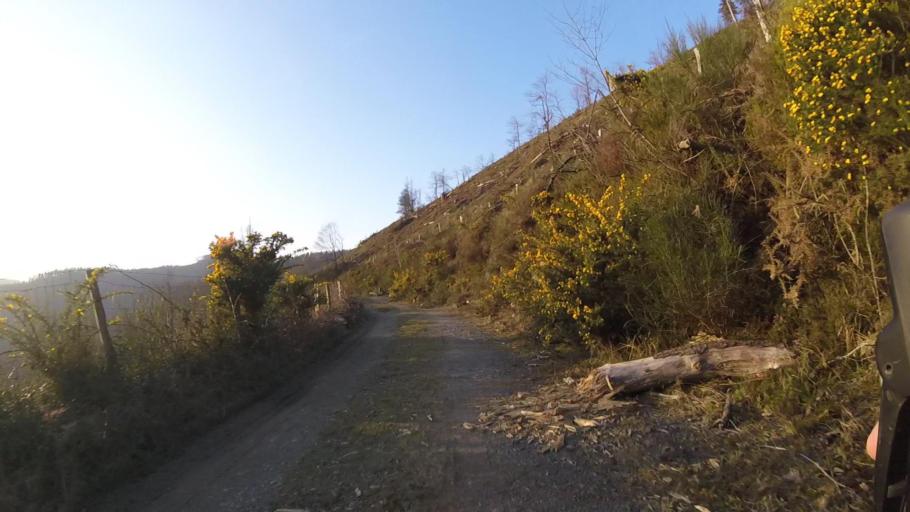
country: ES
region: Navarre
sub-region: Provincia de Navarra
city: Arano
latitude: 43.2486
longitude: -1.8572
